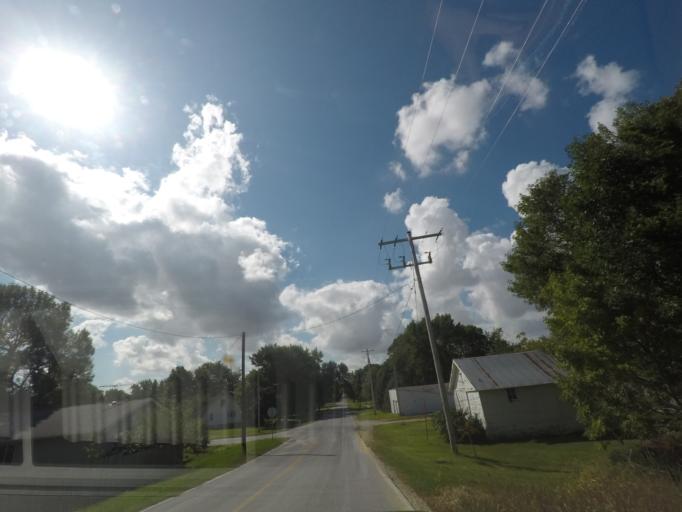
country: US
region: Iowa
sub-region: Story County
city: Nevada
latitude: 42.0190
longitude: -93.3193
